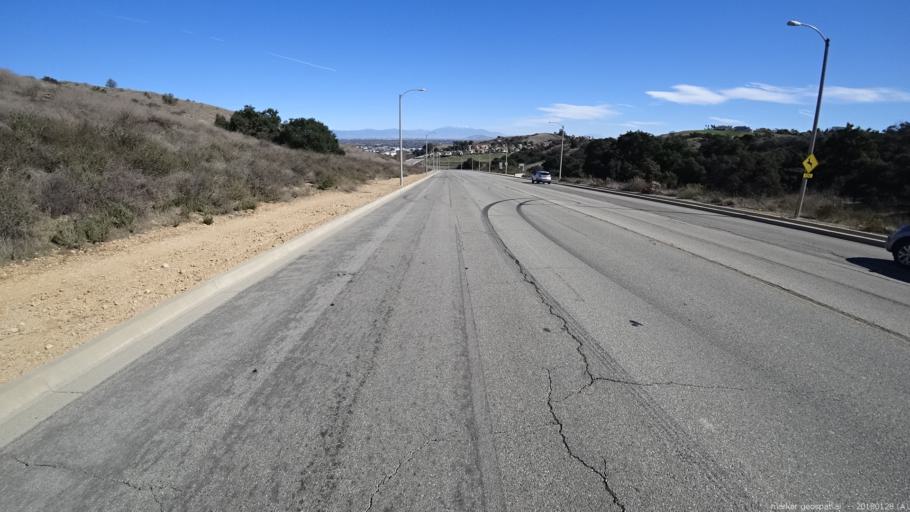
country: US
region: California
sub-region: San Bernardino County
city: Chino Hills
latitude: 34.0137
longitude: -117.7668
